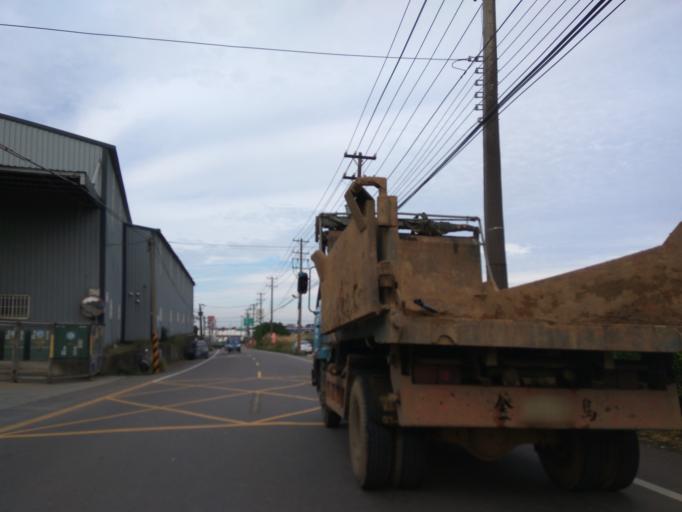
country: TW
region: Taiwan
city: Daxi
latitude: 24.9449
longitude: 121.1492
